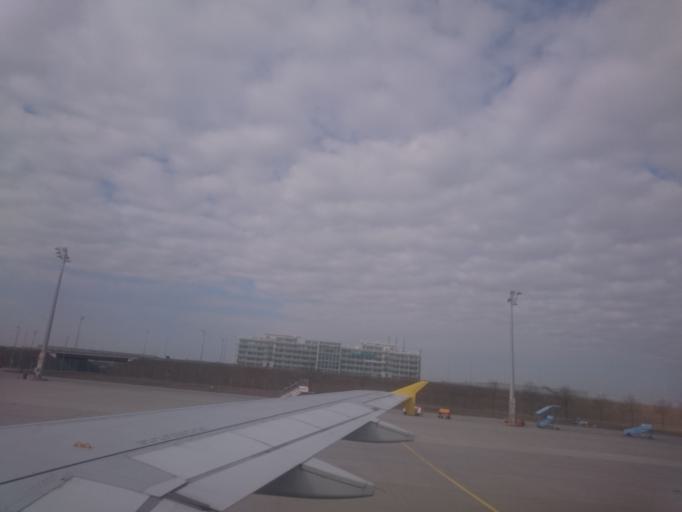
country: DE
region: Bavaria
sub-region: Upper Bavaria
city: Hallbergmoos
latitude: 48.3506
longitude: 11.7783
